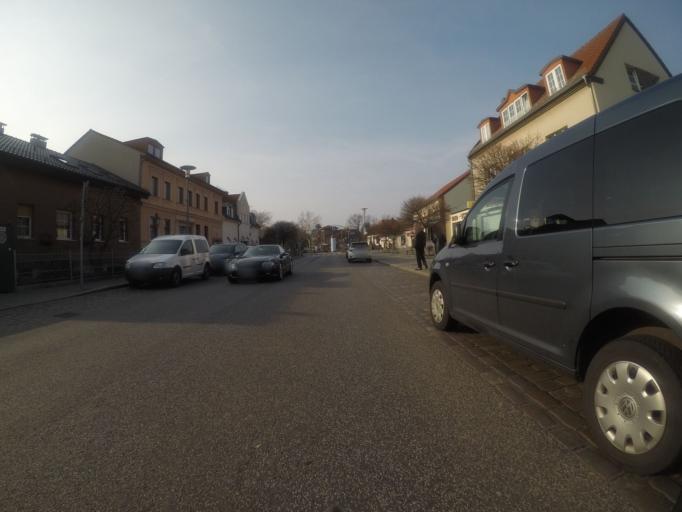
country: DE
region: Berlin
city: Rudow
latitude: 52.4199
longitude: 13.4928
